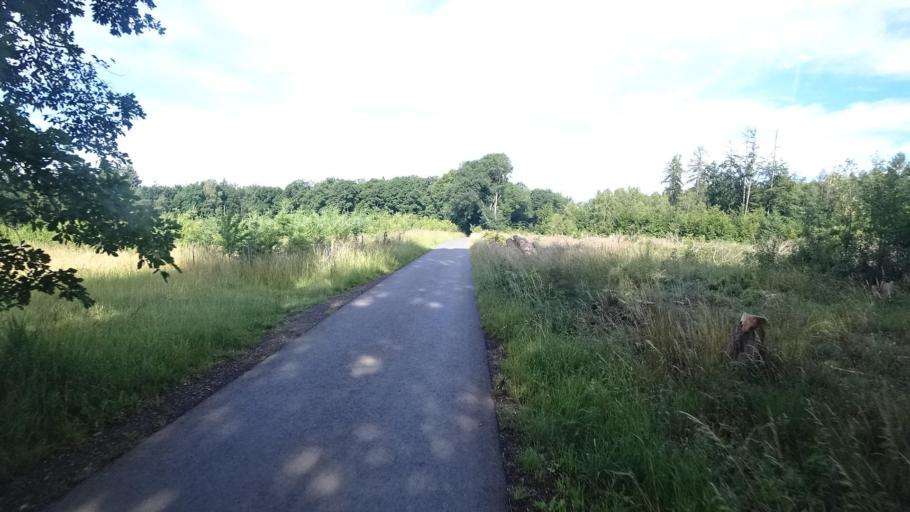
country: DE
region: Rheinland-Pfalz
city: Oberwambach
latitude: 50.6614
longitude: 7.6445
